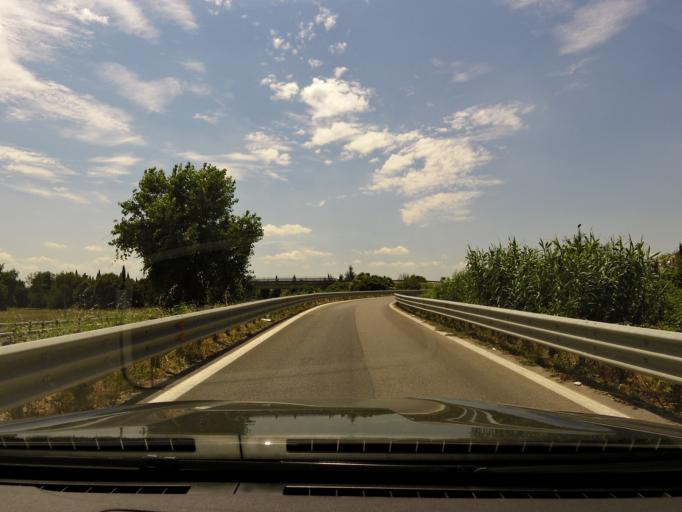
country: IT
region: The Marches
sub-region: Provincia di Pesaro e Urbino
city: Fano
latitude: 43.8244
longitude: 13.0147
